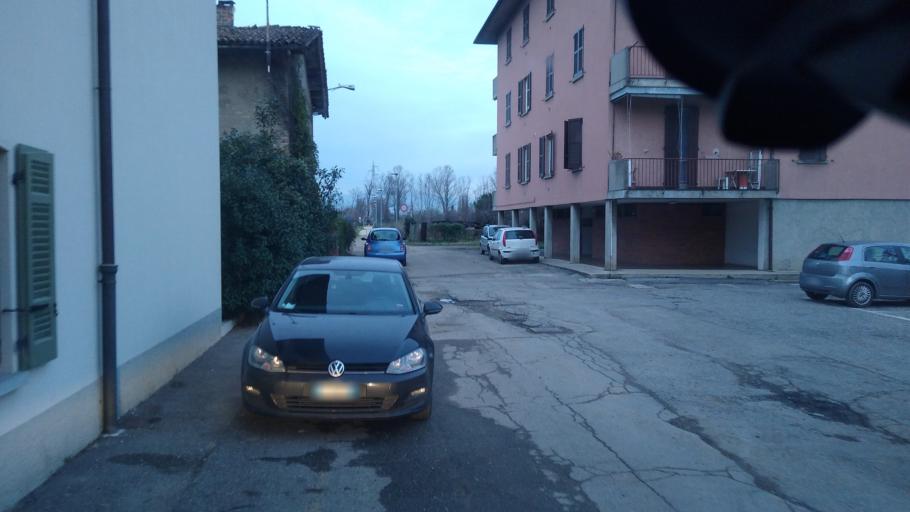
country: IT
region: Lombardy
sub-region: Provincia di Bergamo
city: Geromina
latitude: 45.5511
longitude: 9.5769
